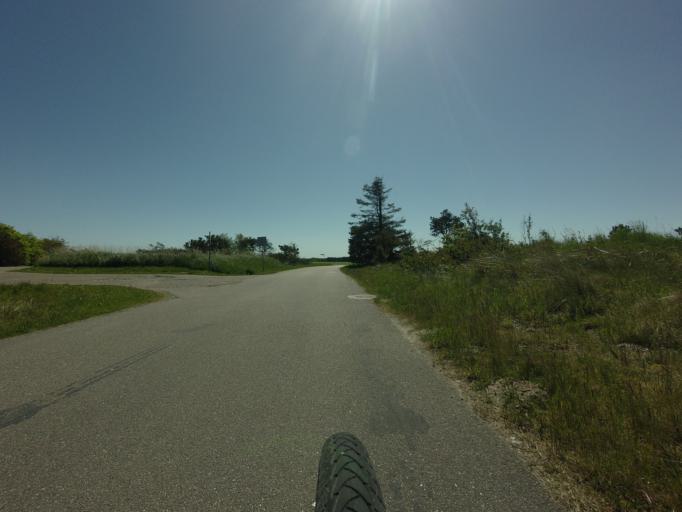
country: DK
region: North Denmark
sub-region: Jammerbugt Kommune
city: Kas
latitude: 57.2205
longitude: 9.5769
